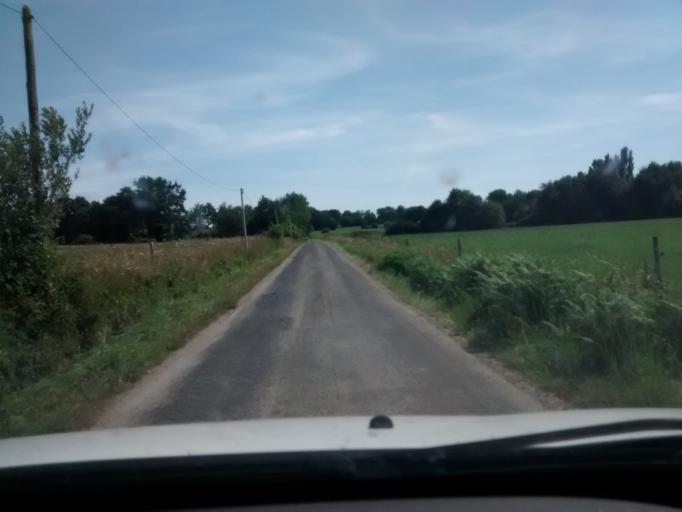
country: FR
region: Brittany
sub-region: Departement d'Ille-et-Vilaine
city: Cesson-Sevigne
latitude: 48.1030
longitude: -1.5987
